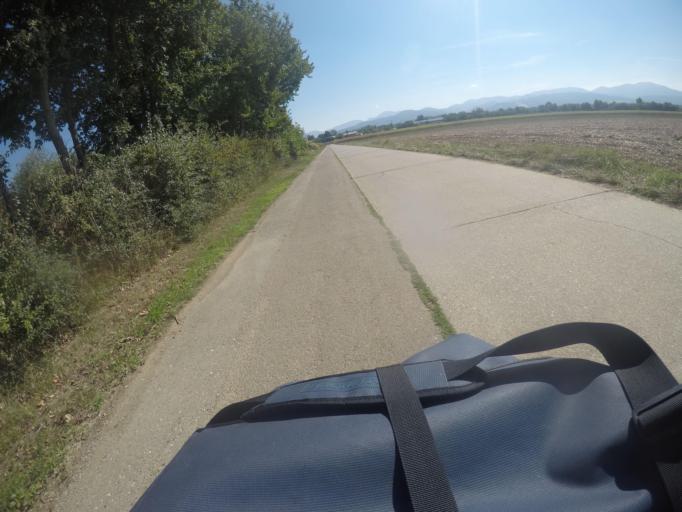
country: DE
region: Baden-Wuerttemberg
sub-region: Freiburg Region
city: Heitersheim
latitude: 47.8764
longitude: 7.6380
